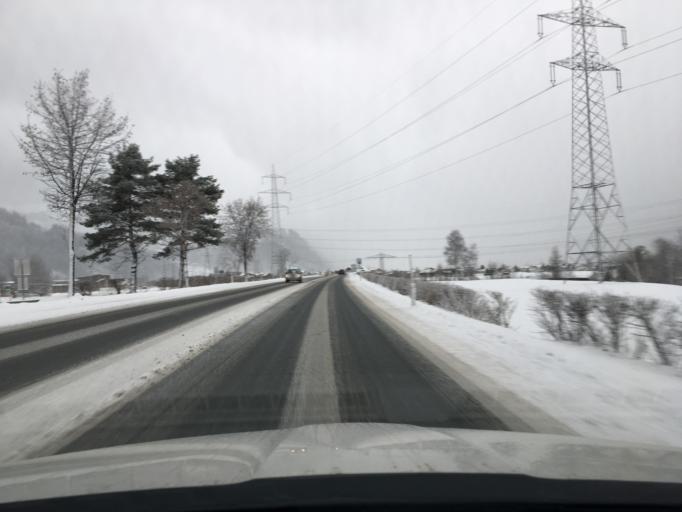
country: AT
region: Tyrol
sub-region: Politischer Bezirk Schwaz
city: Zell am Ziller
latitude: 47.2424
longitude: 11.8999
